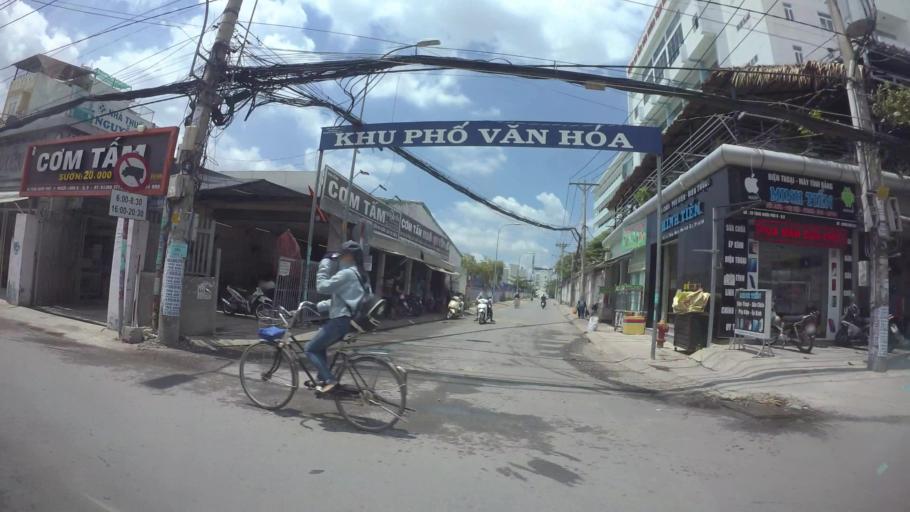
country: VN
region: Ho Chi Minh City
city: Quan Chin
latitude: 10.8306
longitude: 106.7747
